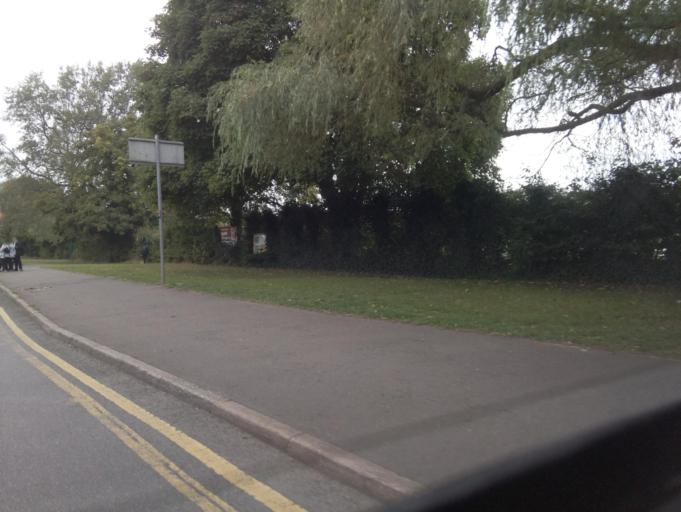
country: GB
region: England
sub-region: South Gloucestershire
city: Severn Beach
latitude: 51.5085
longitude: -2.6323
